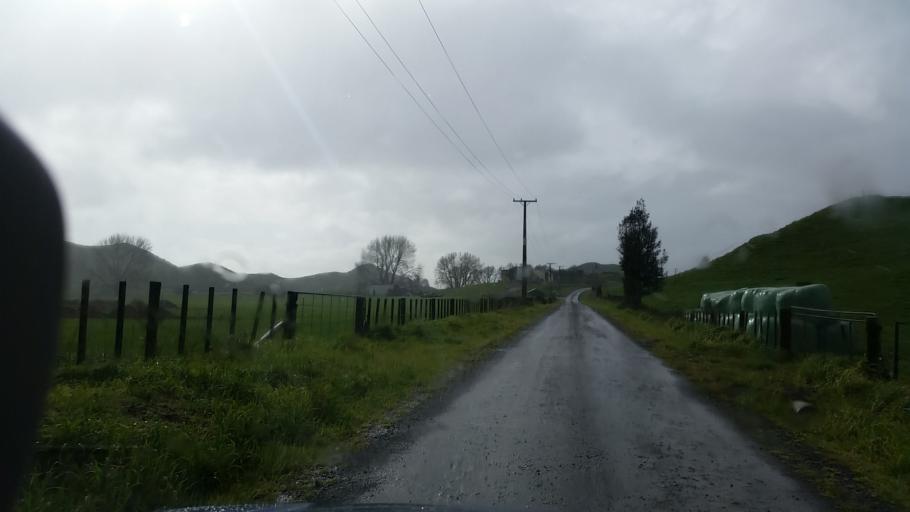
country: NZ
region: Taranaki
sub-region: South Taranaki District
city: Eltham
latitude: -39.3539
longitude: 174.4351
